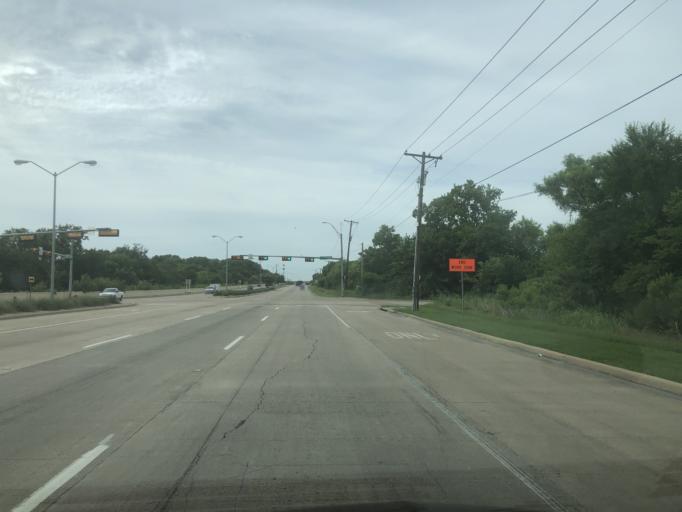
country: US
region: Texas
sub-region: Dallas County
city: Grand Prairie
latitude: 32.7931
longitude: -96.9947
